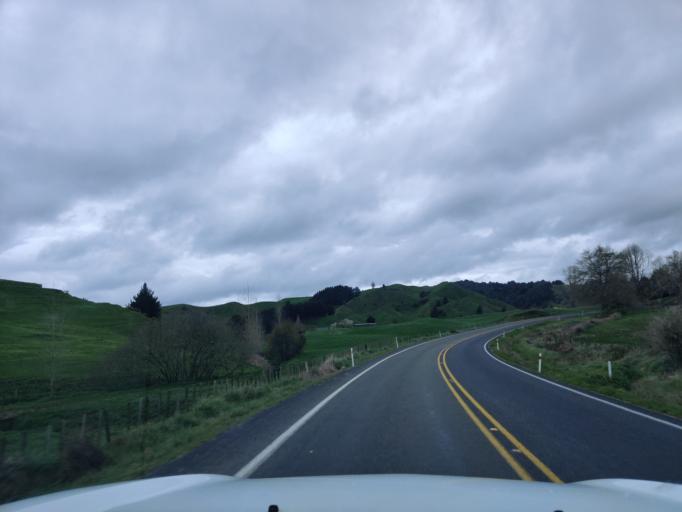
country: NZ
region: Waikato
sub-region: Otorohanga District
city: Otorohanga
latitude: -38.5232
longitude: 175.1760
